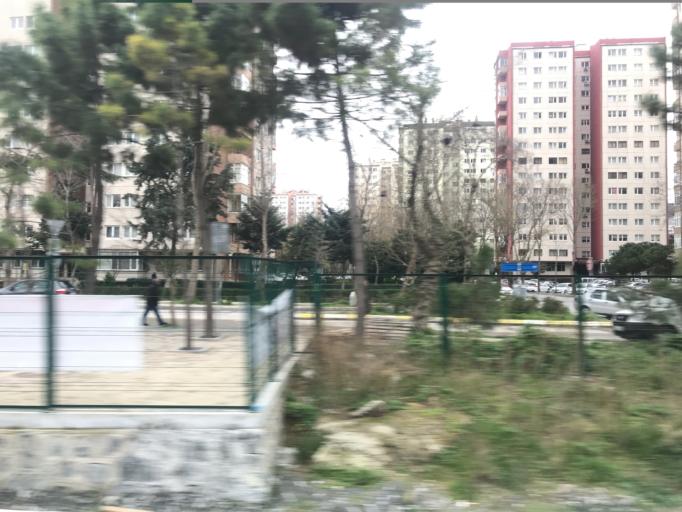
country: TR
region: Istanbul
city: Bahcelievler
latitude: 40.9801
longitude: 28.8517
